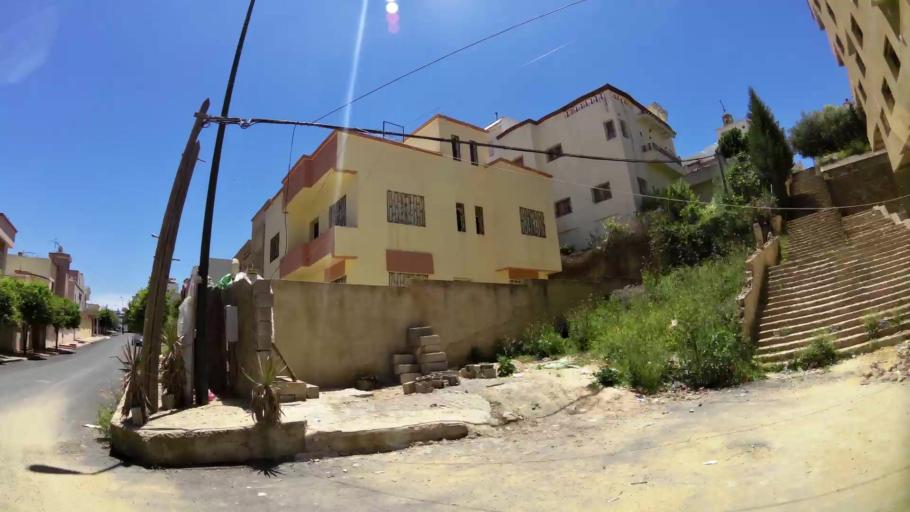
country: MA
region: Meknes-Tafilalet
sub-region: Meknes
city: Meknes
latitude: 33.9080
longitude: -5.5514
